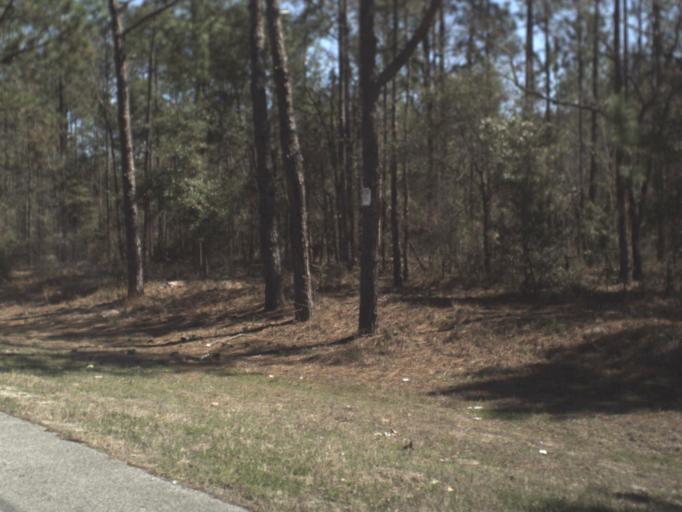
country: US
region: Florida
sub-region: Leon County
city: Woodville
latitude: 30.3095
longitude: -84.3435
